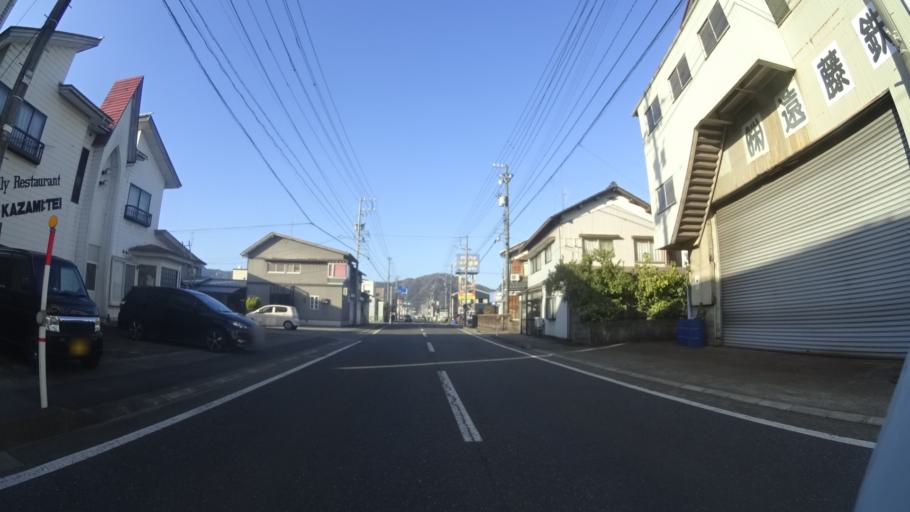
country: JP
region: Fukui
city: Ono
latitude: 35.9896
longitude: 136.4996
